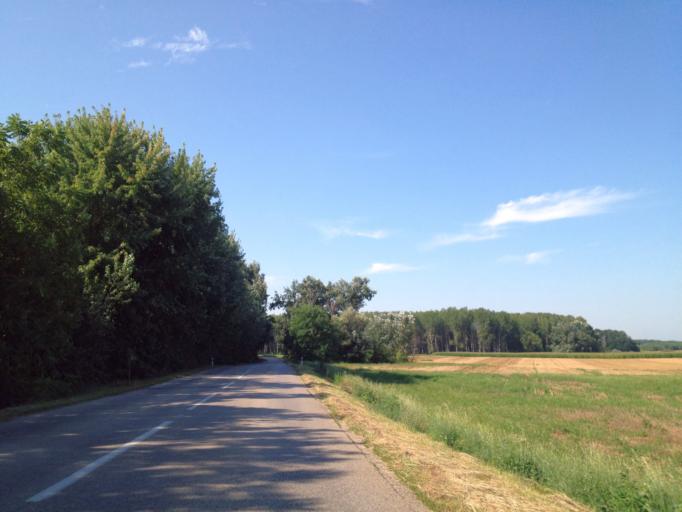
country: SK
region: Nitriansky
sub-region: Okres Komarno
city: Hurbanovo
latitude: 47.8309
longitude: 18.2372
